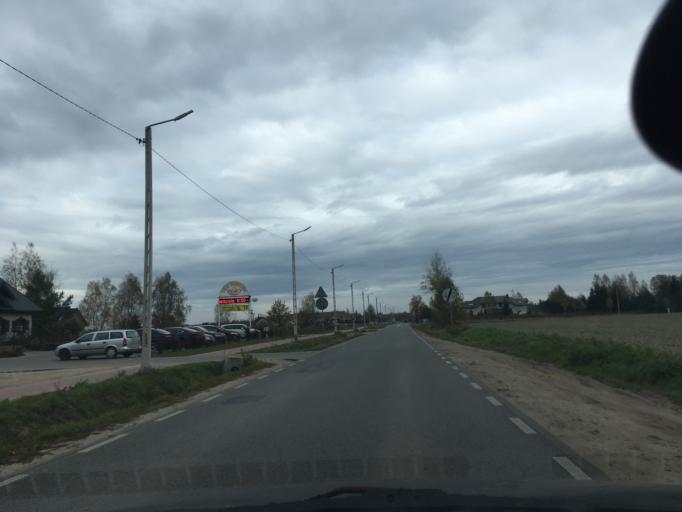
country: PL
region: Lodz Voivodeship
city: Zabia Wola
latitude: 52.0187
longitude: 20.7309
